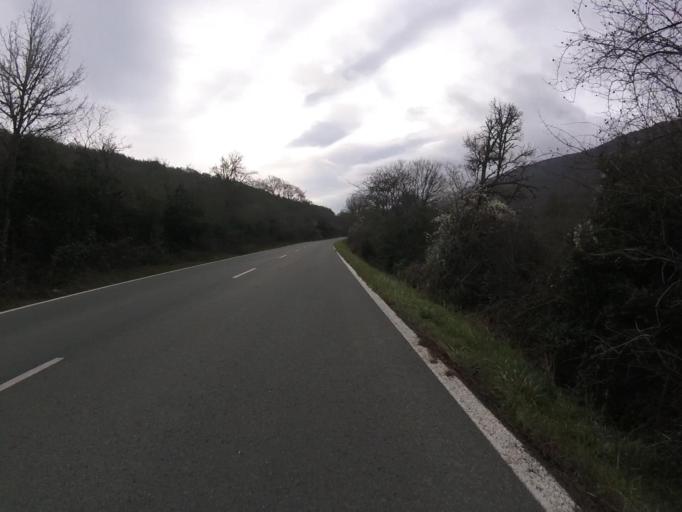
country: ES
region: Navarre
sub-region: Provincia de Navarra
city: Lezaun
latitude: 42.8322
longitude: -2.0278
